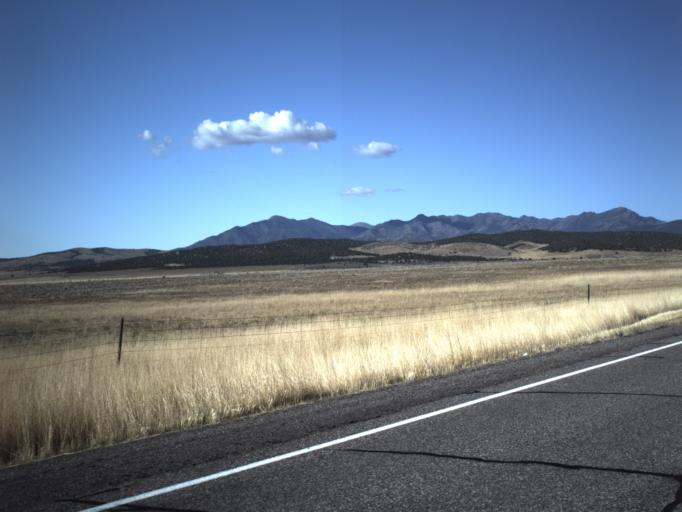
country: US
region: Utah
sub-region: Millard County
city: Fillmore
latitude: 39.1329
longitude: -112.2483
